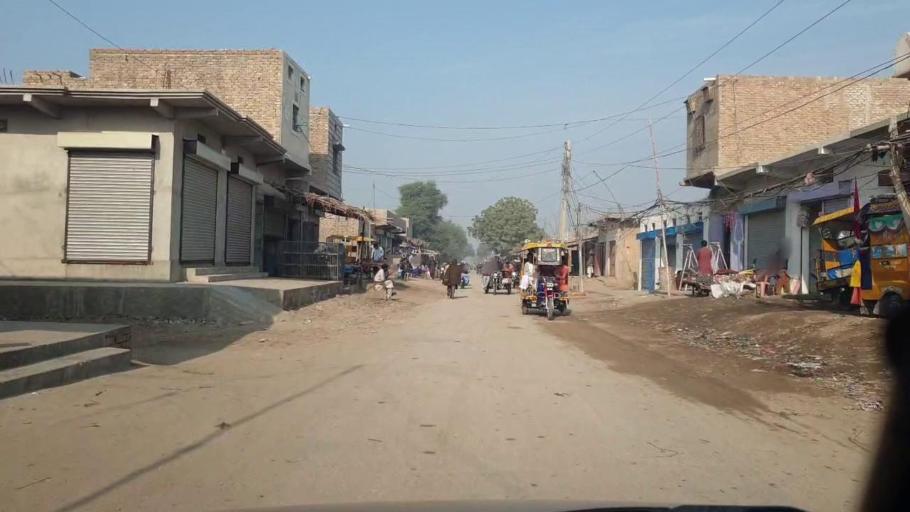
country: PK
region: Sindh
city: Shahdadpur
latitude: 25.9301
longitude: 68.6143
